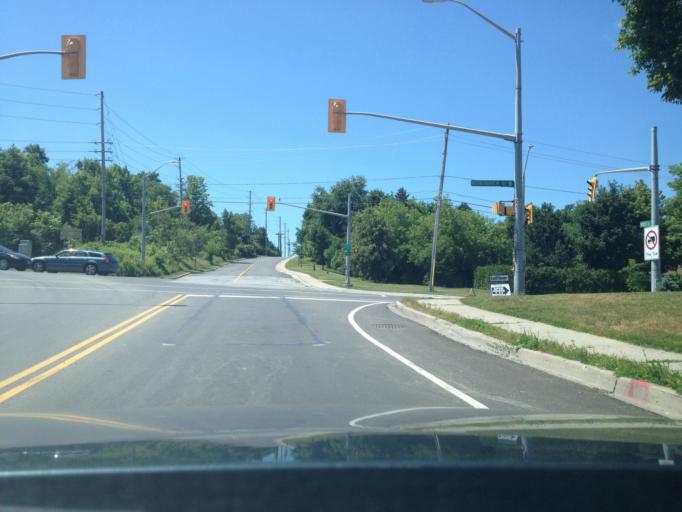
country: CA
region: Ontario
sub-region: Halton
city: Milton
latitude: 43.6591
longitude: -79.9146
